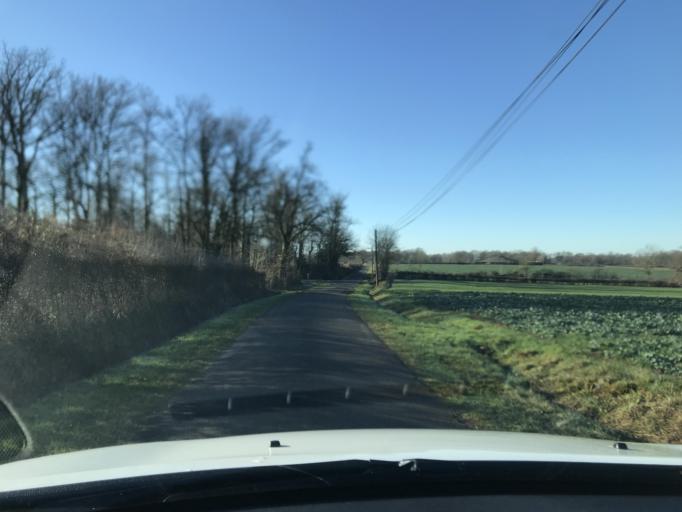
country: FR
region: Poitou-Charentes
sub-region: Departement de la Charente
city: Loubert
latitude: 45.8449
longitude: 0.5423
